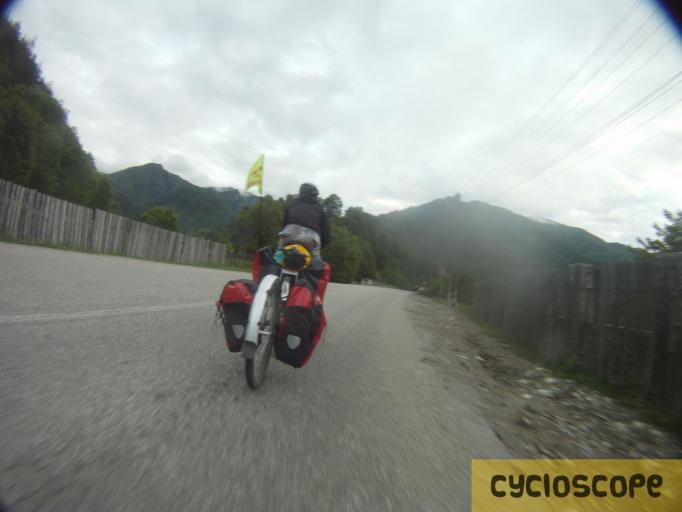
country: RO
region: Valcea
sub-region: Comuna Brezoi
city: Brezoi
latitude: 45.3525
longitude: 24.1930
